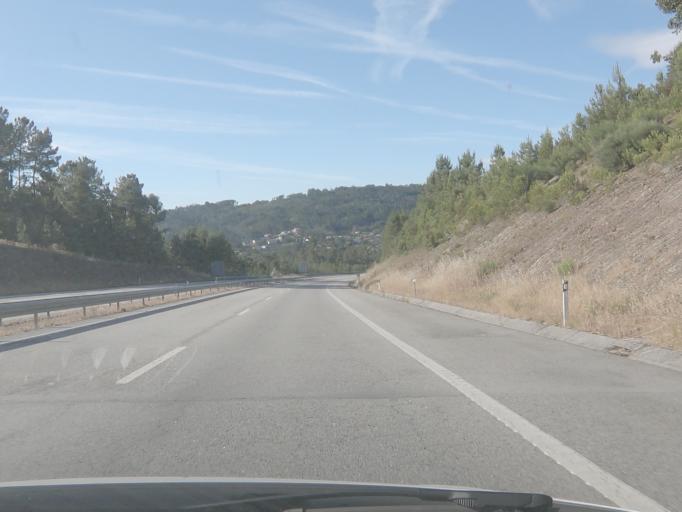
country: PT
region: Viseu
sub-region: Viseu
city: Campo
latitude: 40.7909
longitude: -7.9285
